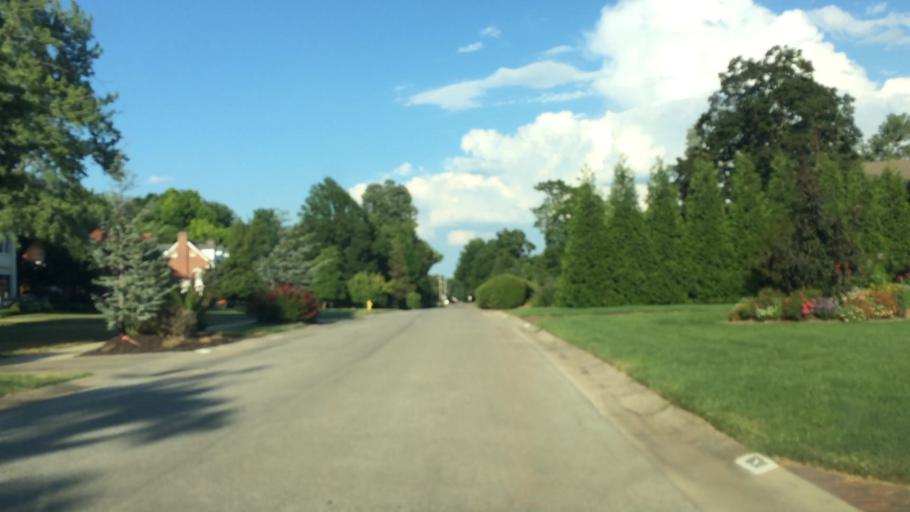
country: US
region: Missouri
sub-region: Greene County
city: Springfield
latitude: 37.1946
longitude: -93.2661
